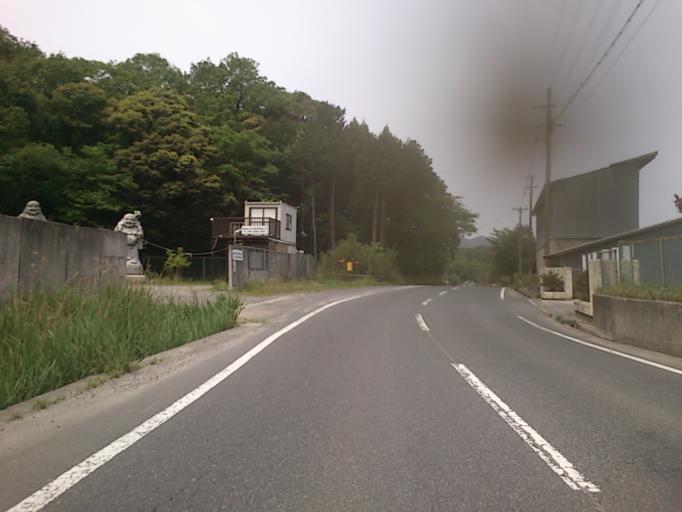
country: JP
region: Kyoto
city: Miyazu
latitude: 35.5957
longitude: 135.0708
